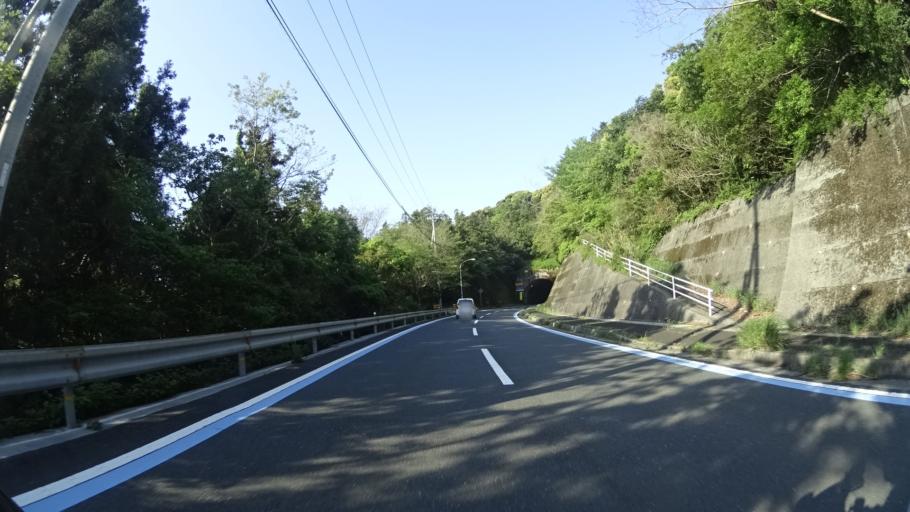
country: JP
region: Ehime
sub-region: Nishiuwa-gun
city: Ikata-cho
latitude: 33.4180
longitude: 132.1830
